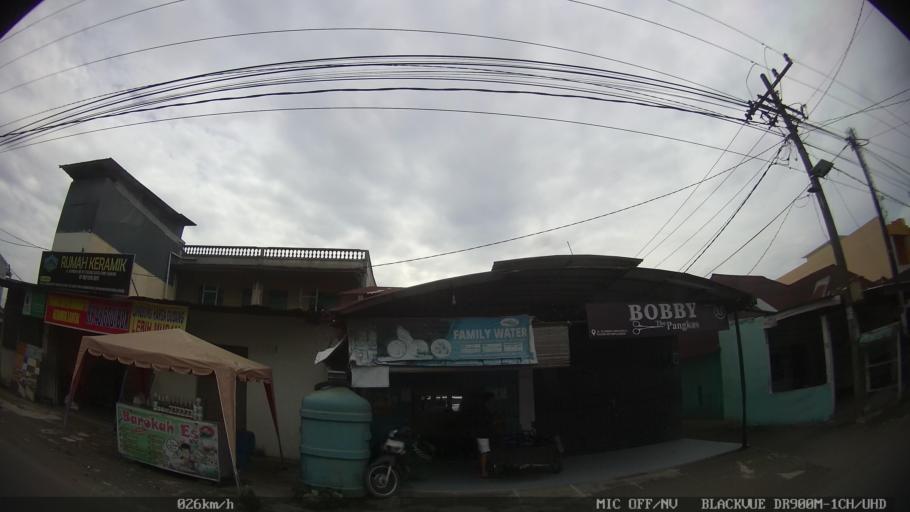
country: ID
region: North Sumatra
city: Sunggal
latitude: 3.6325
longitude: 98.5941
